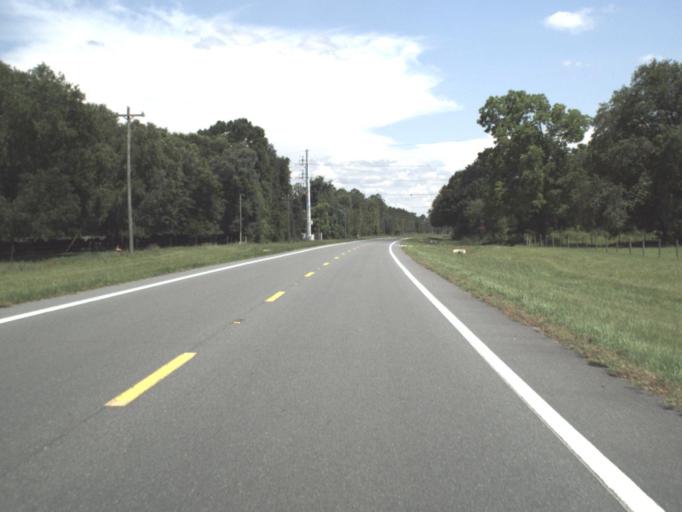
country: US
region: Florida
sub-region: Lafayette County
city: Mayo
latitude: 30.1228
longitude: -83.2673
